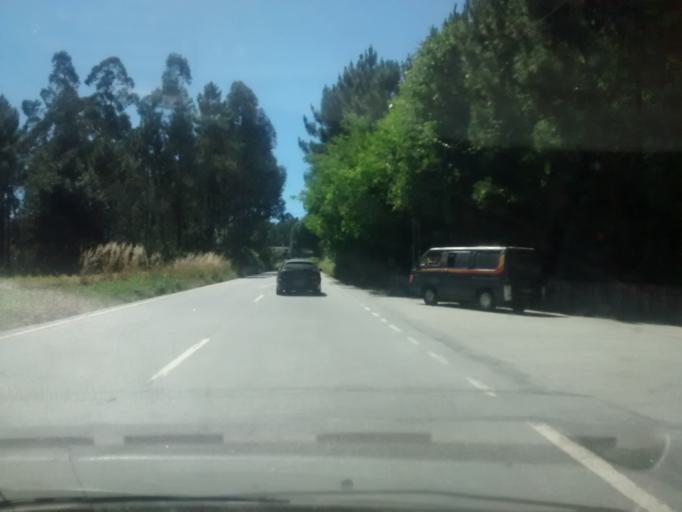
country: PT
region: Braga
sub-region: Barcelos
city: Galegos
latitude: 41.5321
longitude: -8.5507
